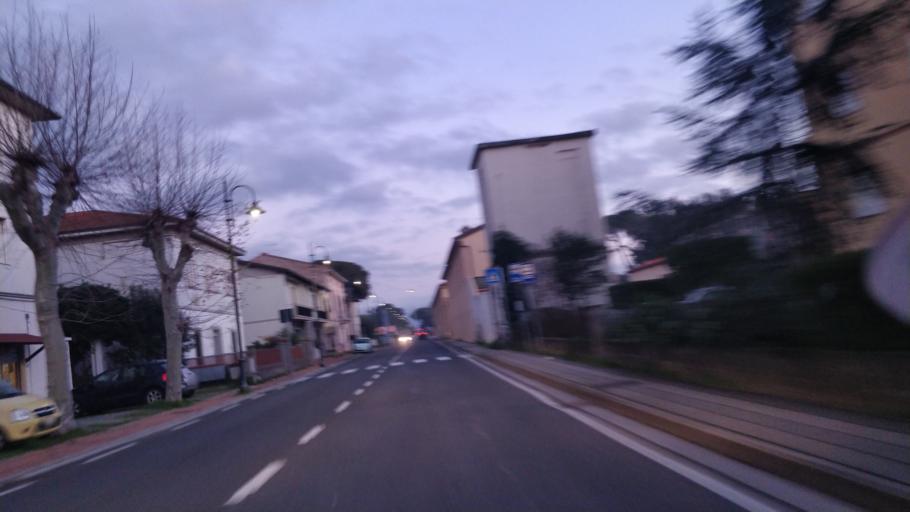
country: IT
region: Tuscany
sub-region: Provincia di Livorno
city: Vada
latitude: 43.3506
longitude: 10.4594
